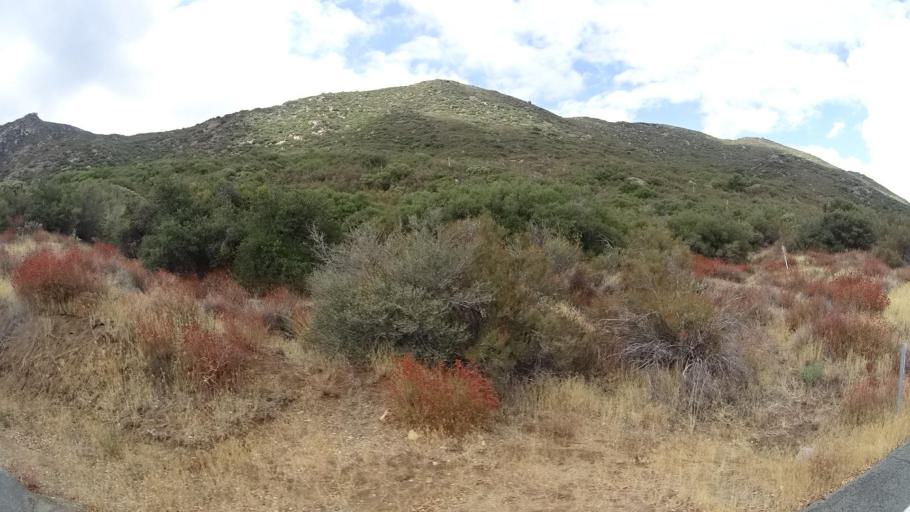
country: US
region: California
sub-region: San Diego County
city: Pine Valley
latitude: 32.7867
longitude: -116.4513
